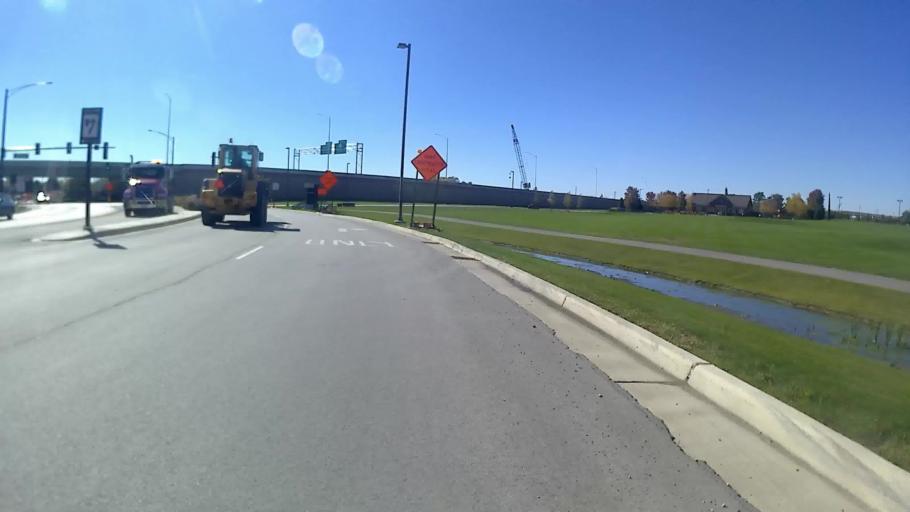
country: US
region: Illinois
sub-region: DuPage County
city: Itasca
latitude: 41.9853
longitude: -88.0123
